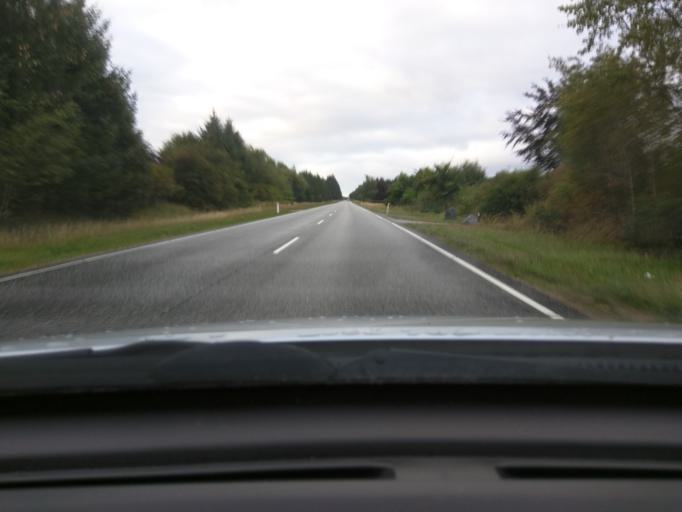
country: DK
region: Central Jutland
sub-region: Ikast-Brande Kommune
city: Bording Kirkeby
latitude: 56.2245
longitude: 9.3193
